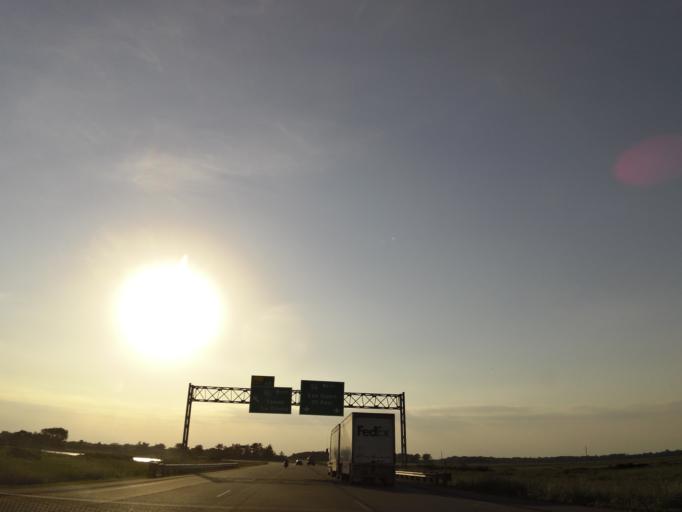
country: US
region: Wisconsin
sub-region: Monroe County
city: Tomah
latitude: 43.9848
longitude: -90.4363
